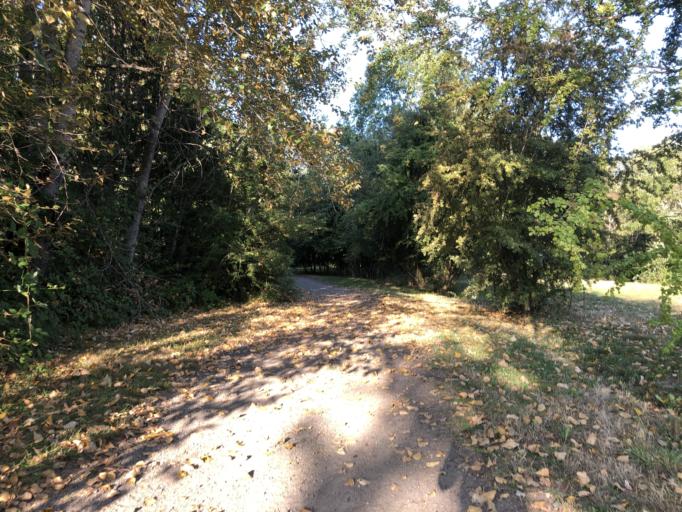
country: US
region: Washington
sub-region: Pierce County
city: Bonney Lake
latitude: 47.2238
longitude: -122.1712
